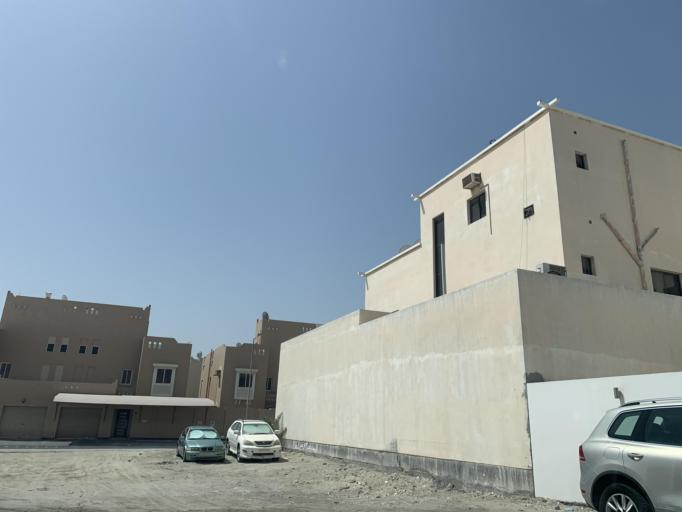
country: BH
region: Muharraq
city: Al Muharraq
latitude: 26.2780
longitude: 50.5982
